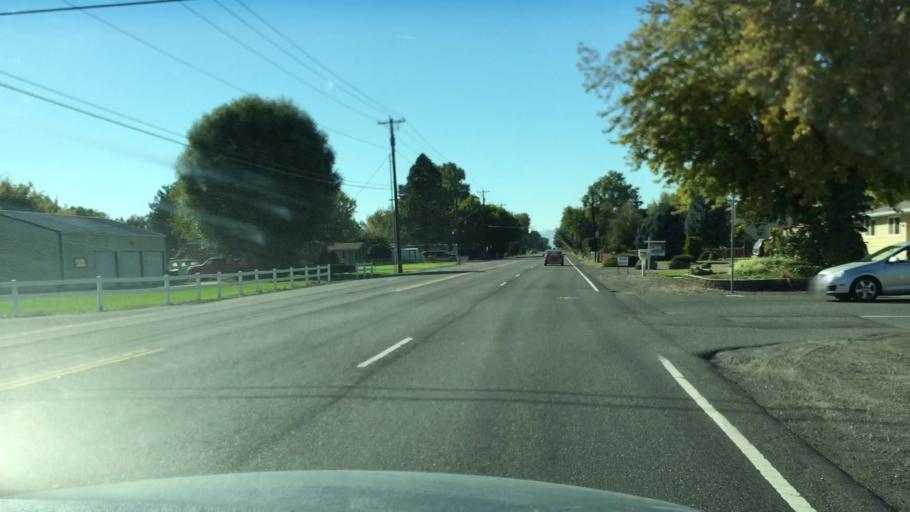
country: US
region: Washington
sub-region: Benton County
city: Kennewick
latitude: 46.2343
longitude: -119.1436
